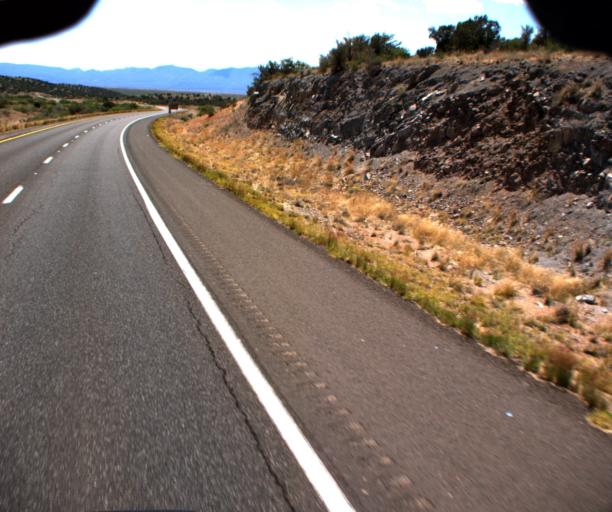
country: US
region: Arizona
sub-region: Yavapai County
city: Cornville
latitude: 34.7987
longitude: -111.9145
